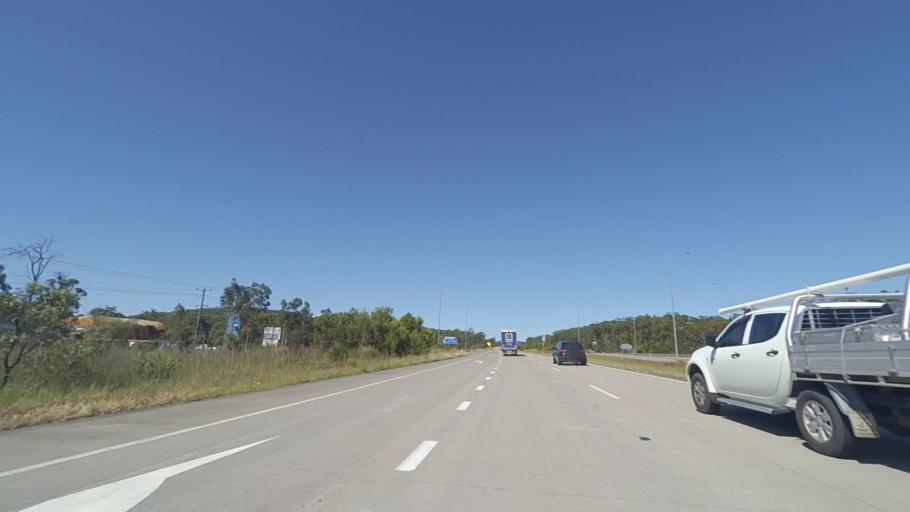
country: AU
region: New South Wales
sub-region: Port Stephens Shire
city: Port Stephens
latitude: -32.6134
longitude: 152.0802
